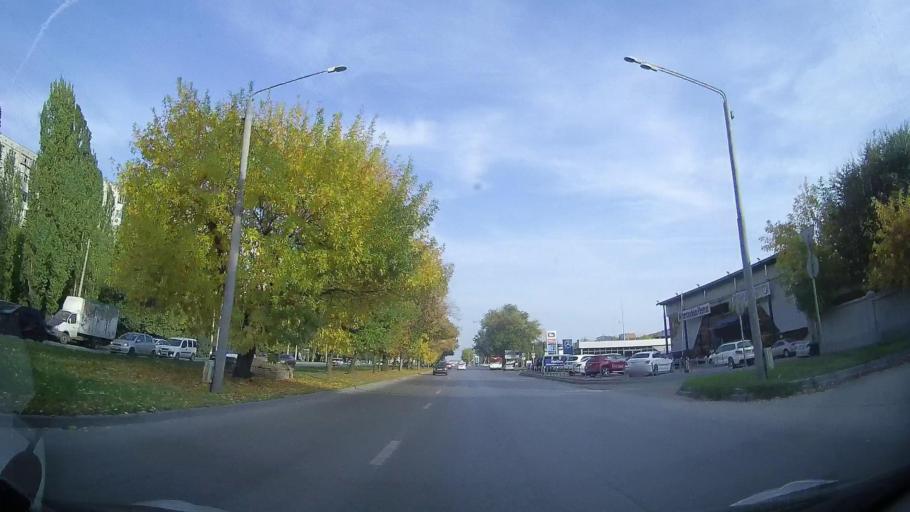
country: RU
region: Rostov
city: Imeni Chkalova
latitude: 47.2806
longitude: 39.7660
